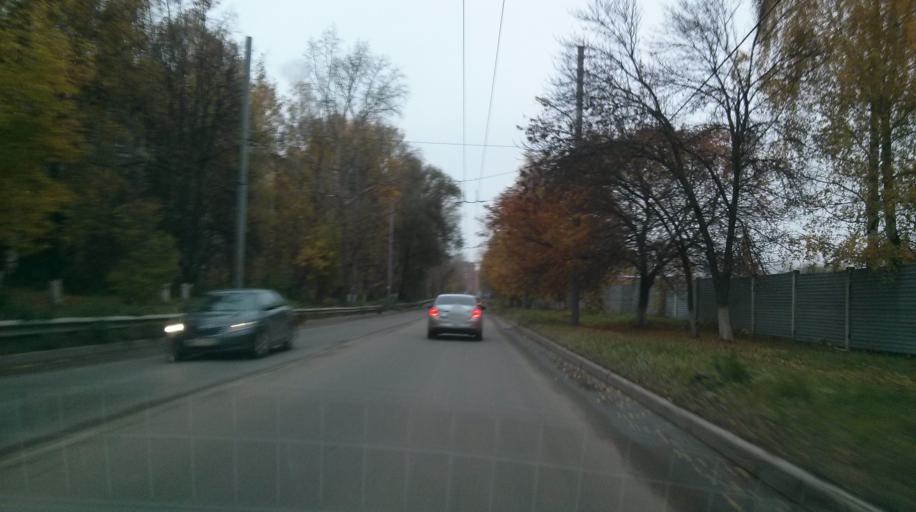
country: RU
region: Nizjnij Novgorod
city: Afonino
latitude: 56.2974
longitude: 44.0509
